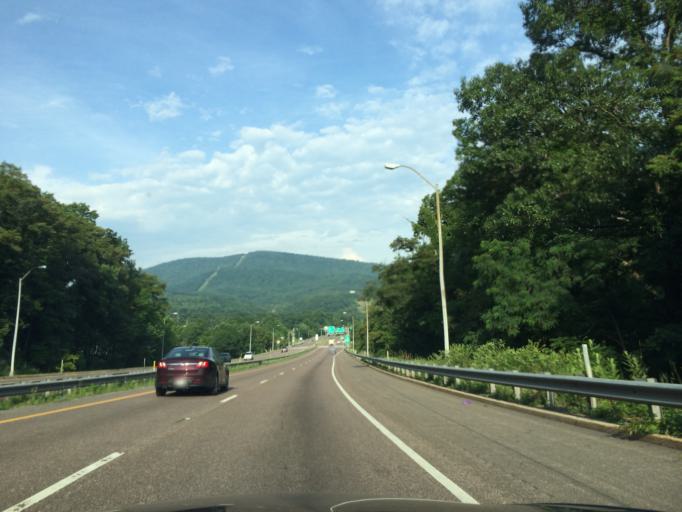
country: US
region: Maryland
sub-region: Allegany County
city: Bowling Green
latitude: 39.6359
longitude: -78.8258
